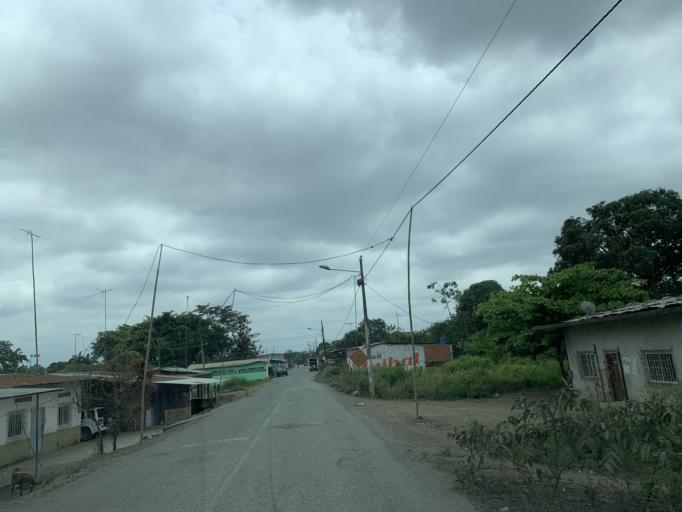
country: EC
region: Guayas
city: Coronel Marcelino Mariduena
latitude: -2.3188
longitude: -79.4704
